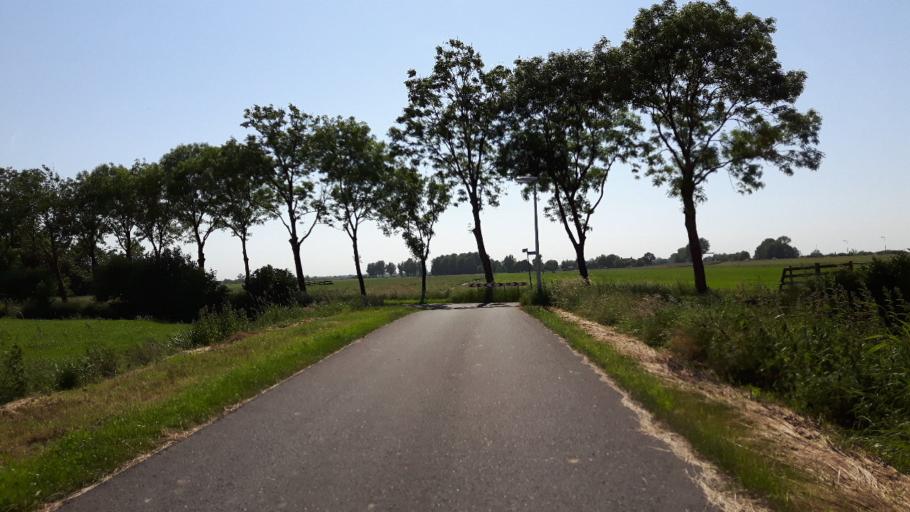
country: NL
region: Utrecht
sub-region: Stichtse Vecht
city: Vreeland
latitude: 52.2211
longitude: 4.9841
